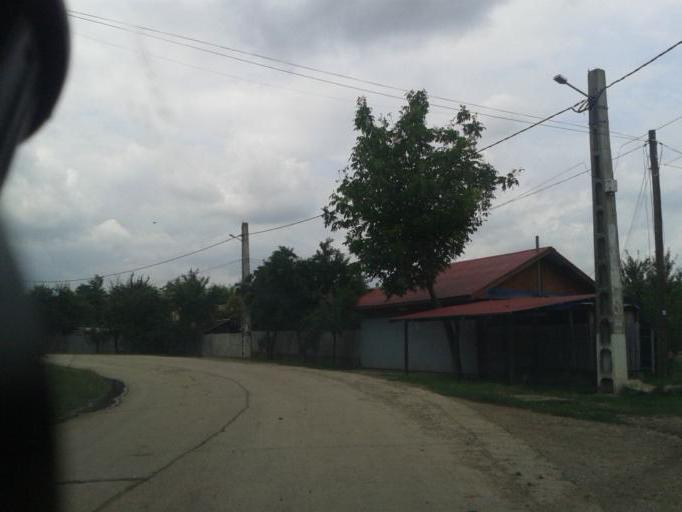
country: RO
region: Ialomita
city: Dragoesti-Snagov
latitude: 44.5350
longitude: 26.4819
